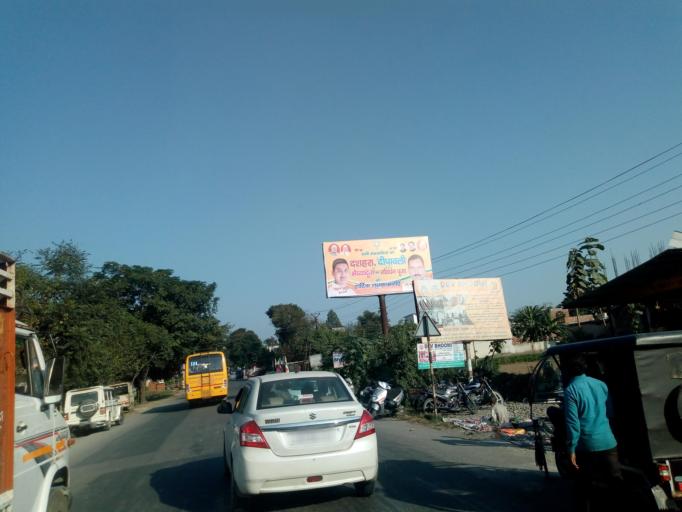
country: IN
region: Uttarakhand
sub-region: Dehradun
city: Dehradun
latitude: 30.3443
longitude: 77.9197
